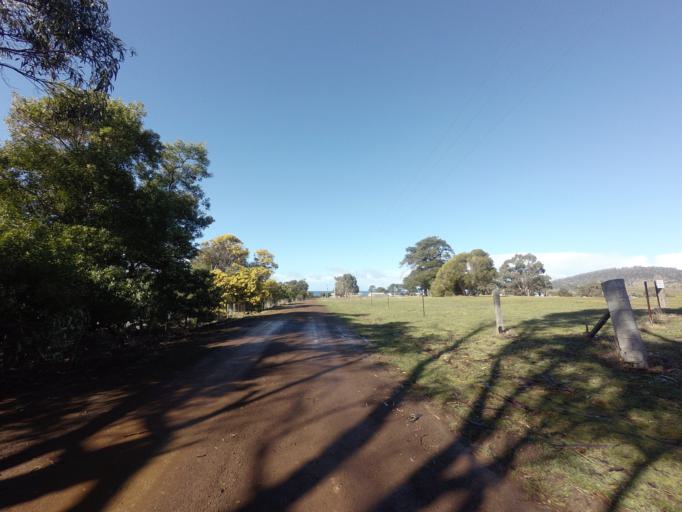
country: AU
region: Tasmania
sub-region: Sorell
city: Sorell
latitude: -42.4013
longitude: 147.9783
